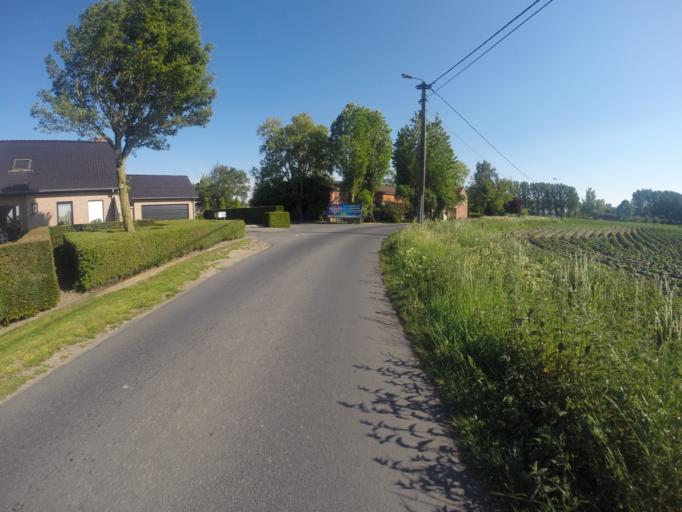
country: BE
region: Flanders
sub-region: Provincie Oost-Vlaanderen
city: Aalter
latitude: 51.0704
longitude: 3.4232
